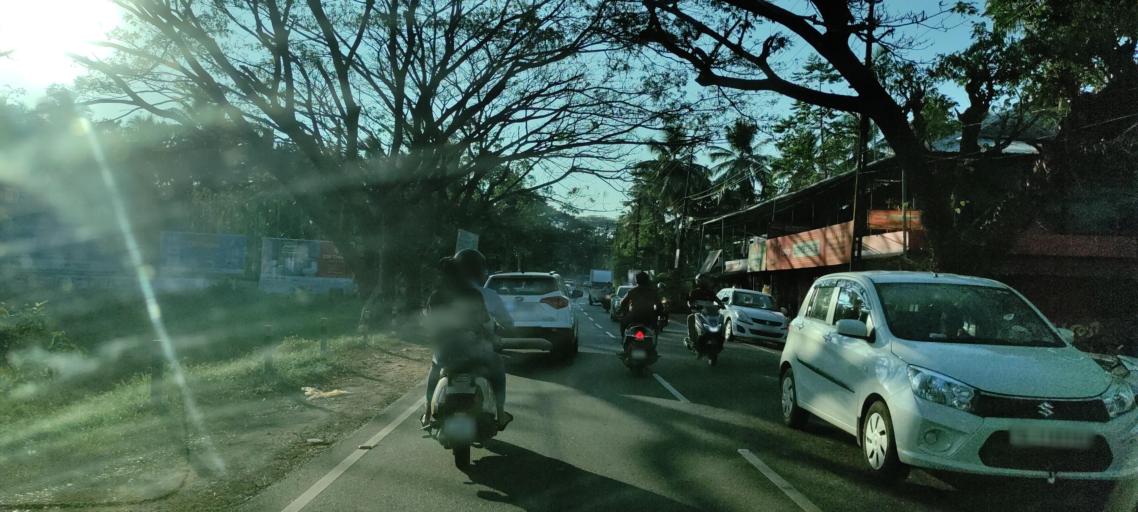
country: IN
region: Kerala
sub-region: Alappuzha
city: Kattanam
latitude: 9.1735
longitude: 76.5850
